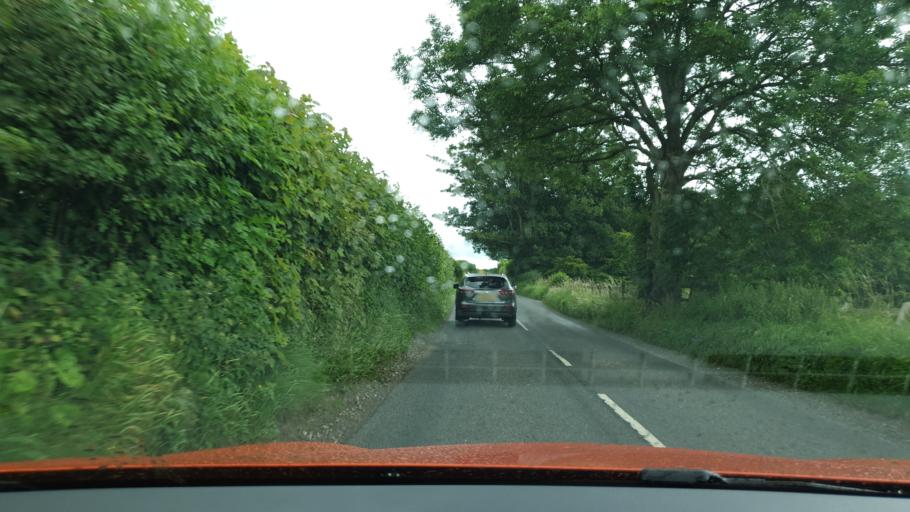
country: GB
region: England
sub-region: Cumbria
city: Penrith
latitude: 54.6209
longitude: -2.8002
